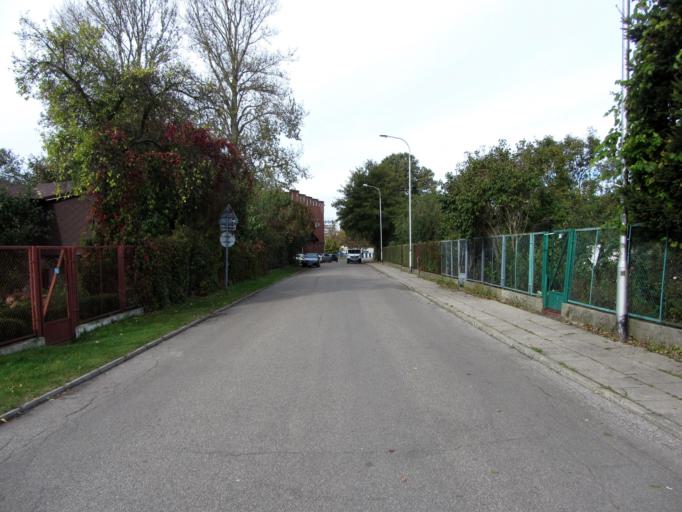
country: PL
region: West Pomeranian Voivodeship
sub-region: Powiat kolobrzeski
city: Kolobrzeg
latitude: 54.1714
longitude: 15.5755
